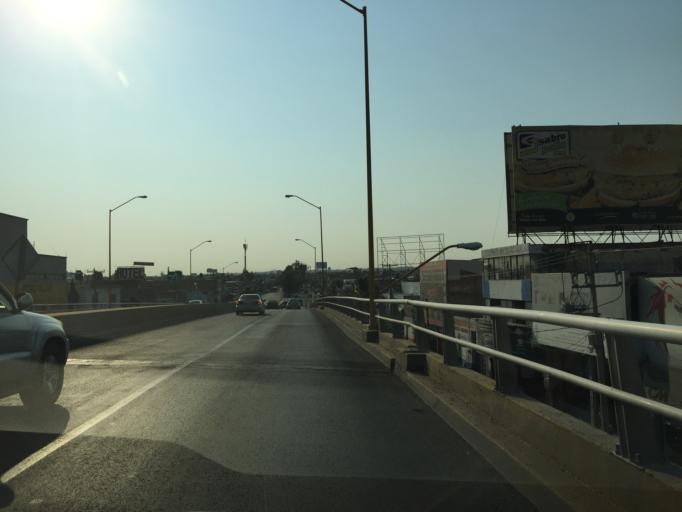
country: MX
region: Aguascalientes
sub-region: Aguascalientes
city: La Loma de los Negritos
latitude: 21.8591
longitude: -102.3137
